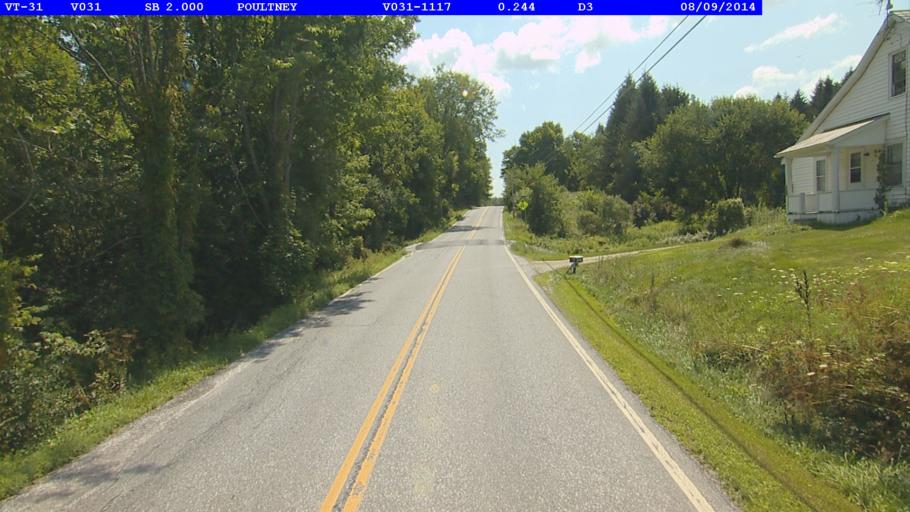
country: US
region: Vermont
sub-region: Rutland County
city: Poultney
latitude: 43.4655
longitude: -73.2431
